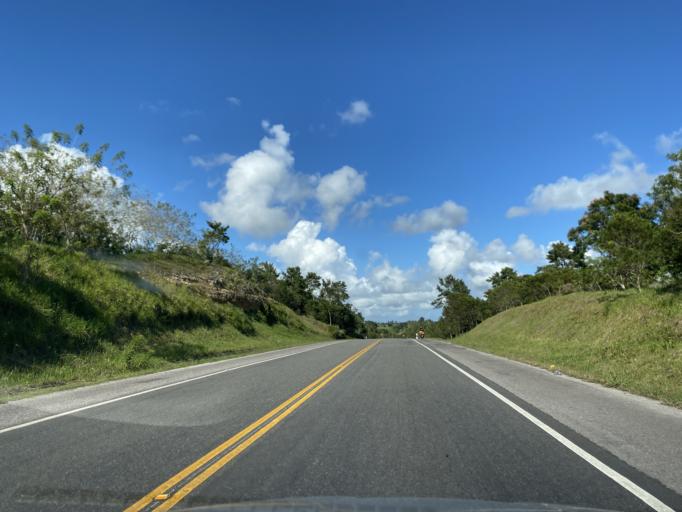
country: DO
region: Monte Plata
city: Majagual
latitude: 19.0177
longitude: -69.8228
